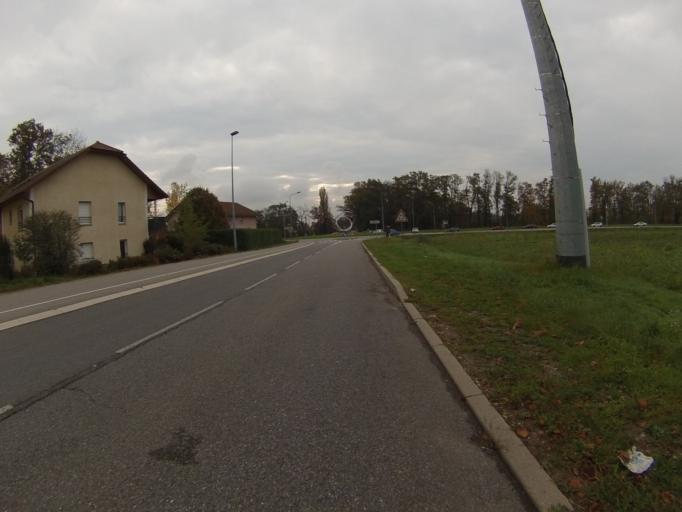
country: CH
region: Geneva
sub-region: Geneva
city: Meyrin
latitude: 46.2470
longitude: 6.0804
